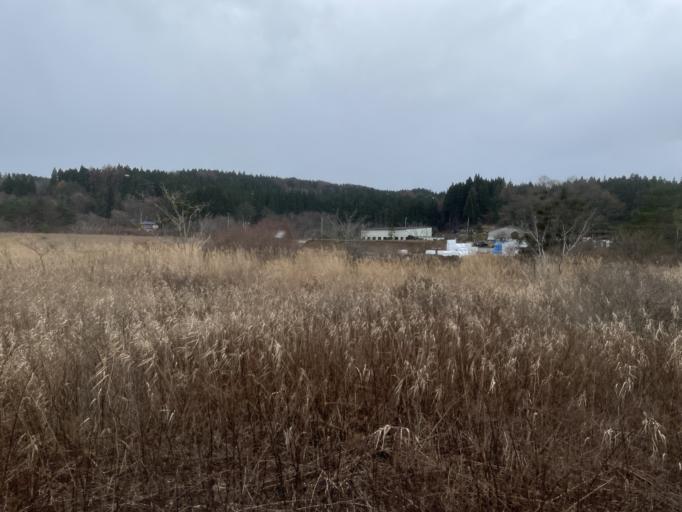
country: JP
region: Aomori
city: Goshogawara
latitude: 41.1760
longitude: 140.4950
